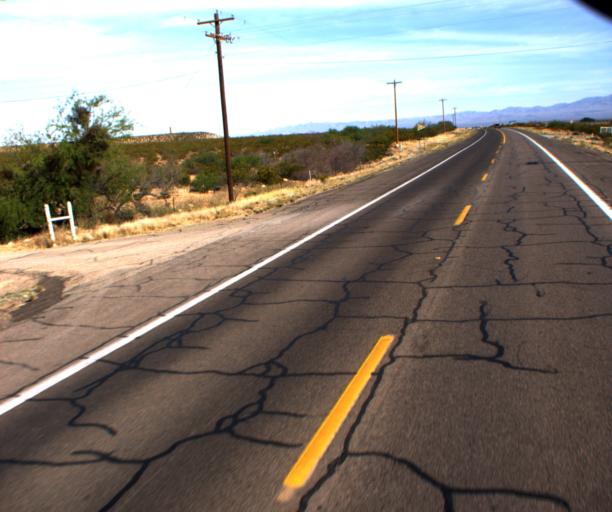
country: US
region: Arizona
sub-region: Graham County
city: Swift Trail Junction
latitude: 32.7114
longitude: -109.7079
